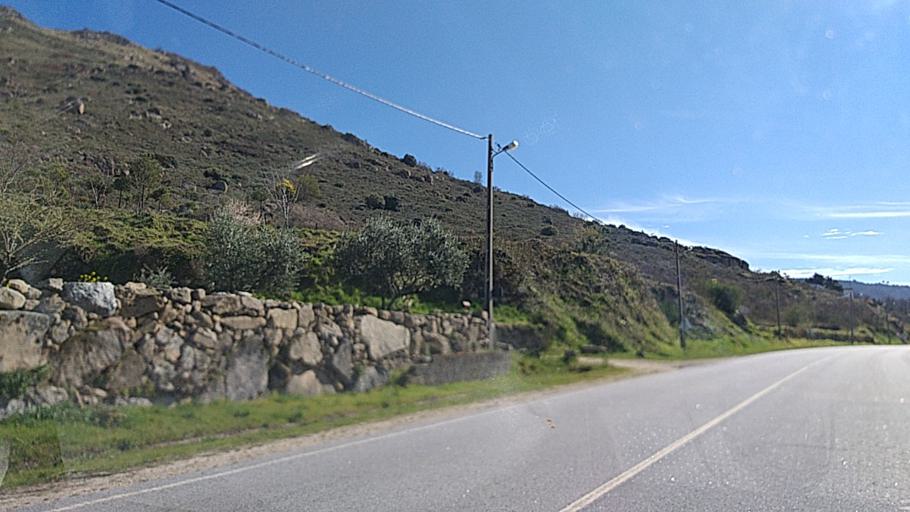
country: PT
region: Guarda
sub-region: Guarda
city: Guarda
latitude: 40.5783
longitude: -7.2952
